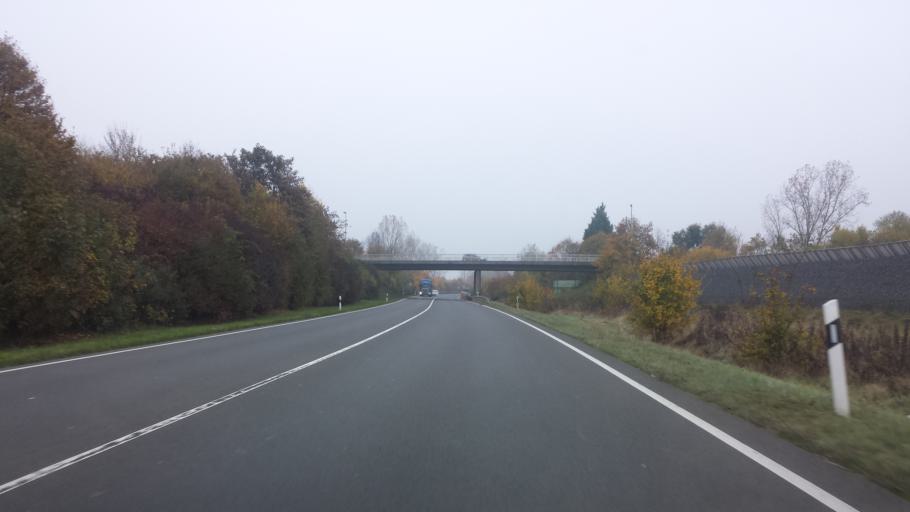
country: DE
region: Hesse
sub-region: Regierungsbezirk Darmstadt
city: Burstadt
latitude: 49.6393
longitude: 8.4750
